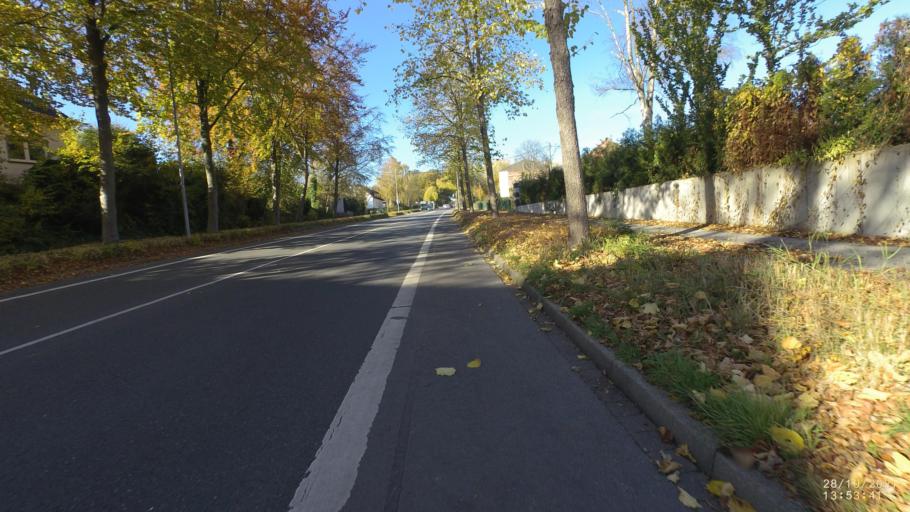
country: DE
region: North Rhine-Westphalia
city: Iserlohn
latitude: 51.3899
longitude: 7.6718
